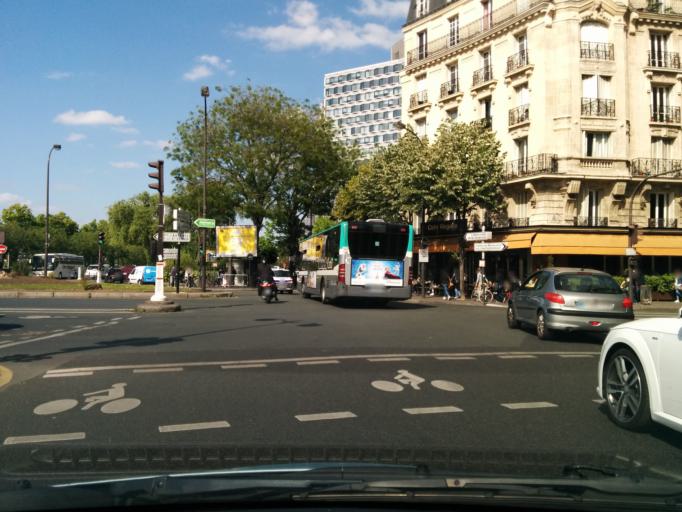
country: FR
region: Ile-de-France
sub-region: Departement des Hauts-de-Seine
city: Issy-les-Moulineaux
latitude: 48.8456
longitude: 2.2772
